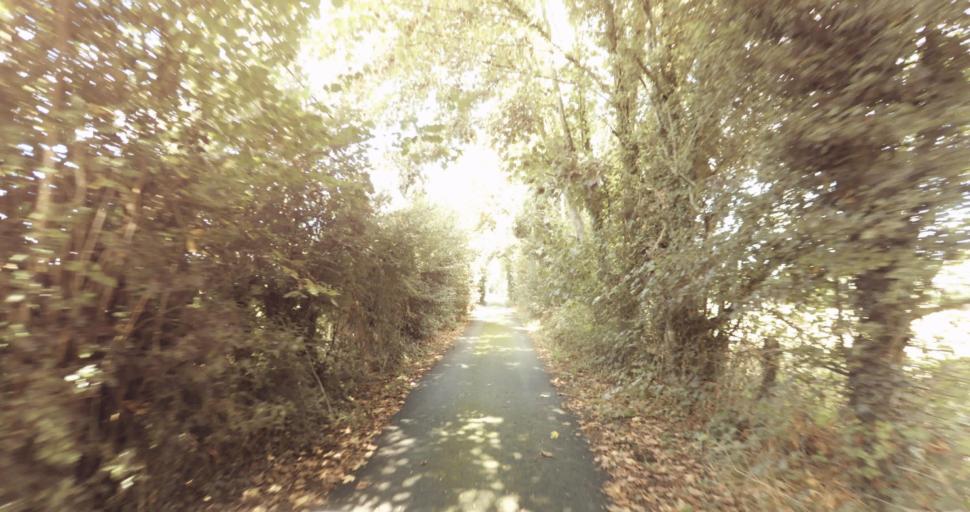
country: FR
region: Lower Normandy
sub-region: Departement de l'Orne
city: Vimoutiers
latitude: 48.9323
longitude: 0.2597
